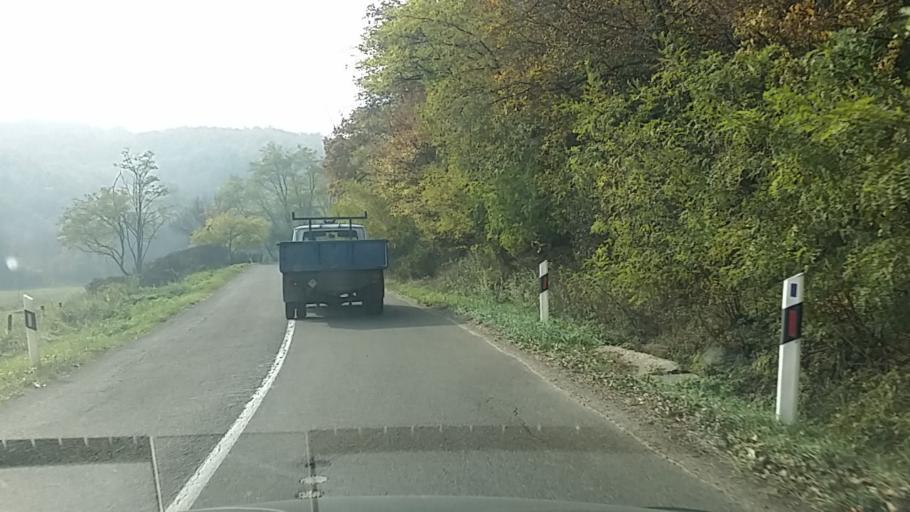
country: HU
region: Pest
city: Veroce
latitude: 47.8323
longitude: 19.0745
